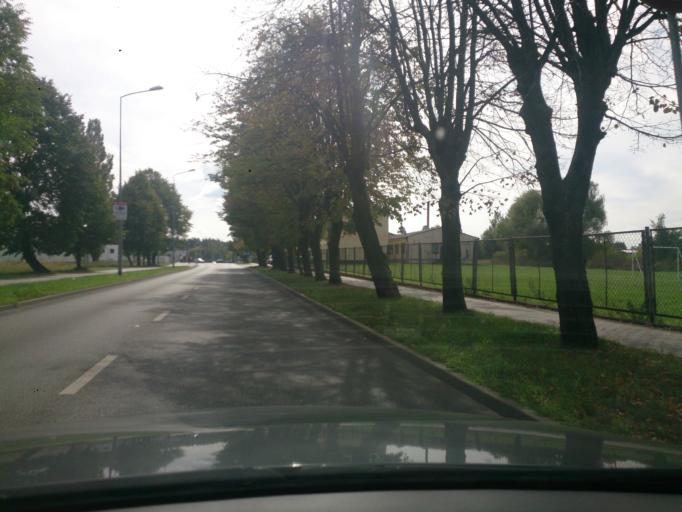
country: PL
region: Kujawsko-Pomorskie
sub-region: Grudziadz
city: Grudziadz
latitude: 53.4706
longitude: 18.7522
